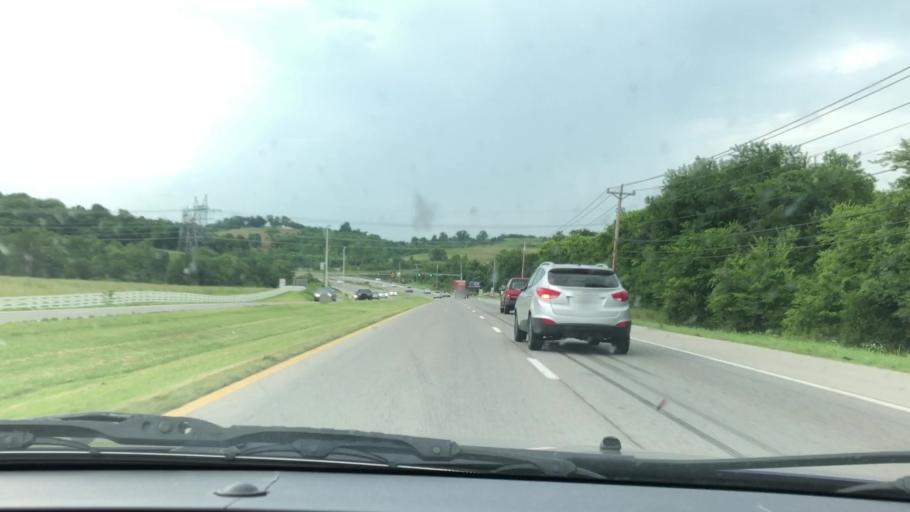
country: US
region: Tennessee
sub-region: Maury County
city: Columbia
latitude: 35.6724
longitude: -87.0027
